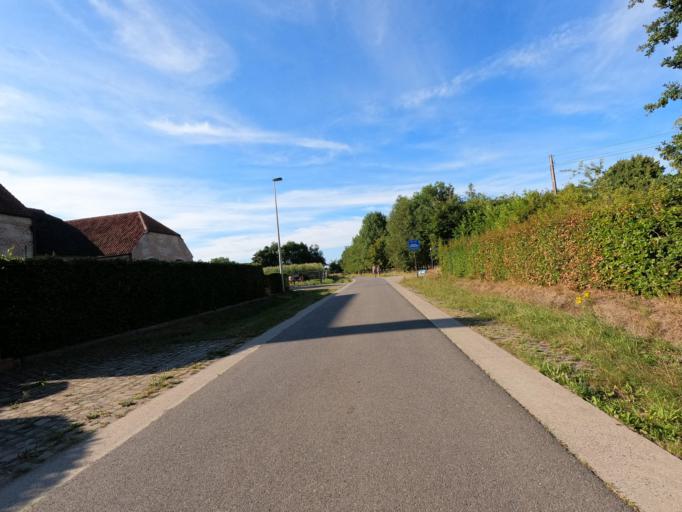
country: BE
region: Flanders
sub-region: Provincie Antwerpen
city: Nijlen
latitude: 51.1357
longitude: 4.6917
